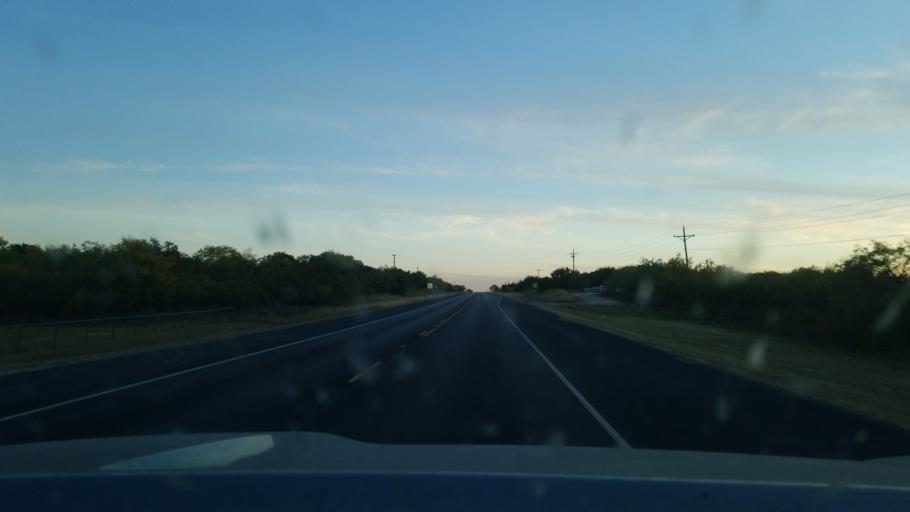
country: US
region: Texas
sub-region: Stephens County
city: Breckenridge
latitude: 32.6901
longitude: -98.9027
